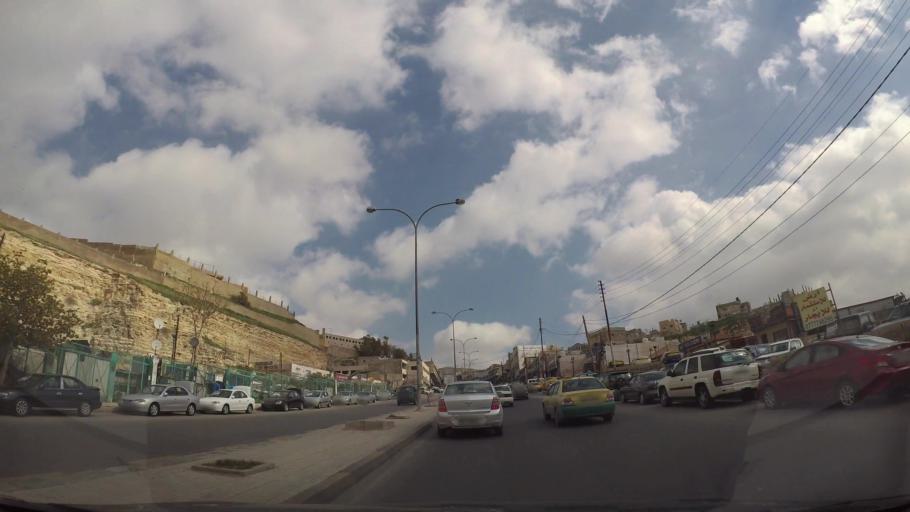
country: JO
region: Amman
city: Al Quwaysimah
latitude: 31.9307
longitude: 35.9294
